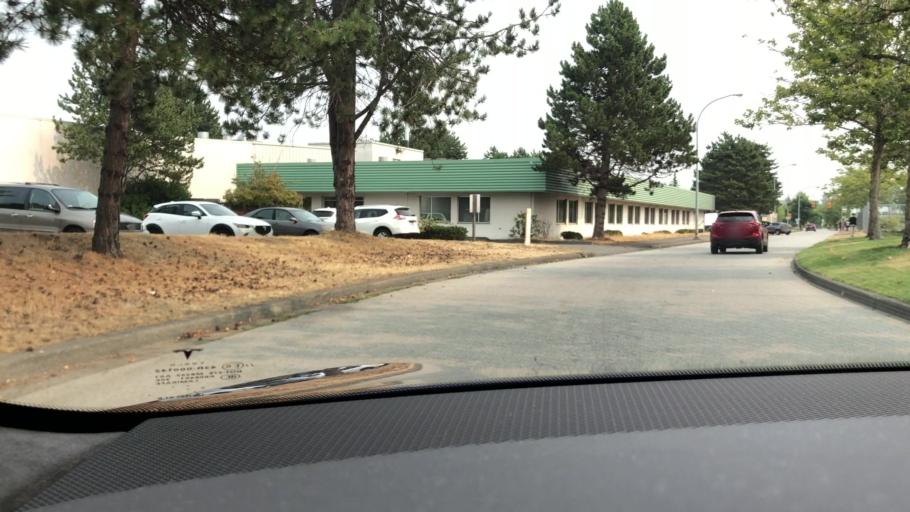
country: CA
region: British Columbia
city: Ladner
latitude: 49.1304
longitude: -123.0950
